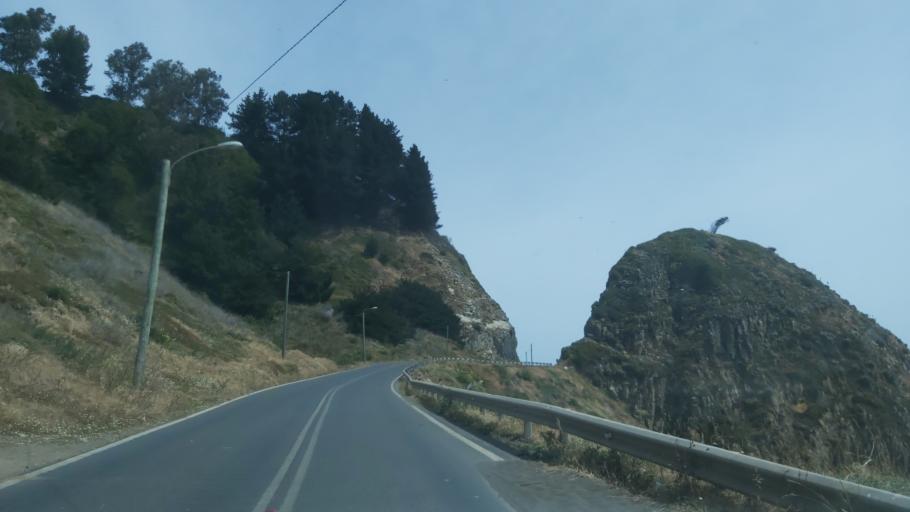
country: CL
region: Maule
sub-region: Provincia de Talca
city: Constitucion
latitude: -35.3296
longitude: -72.4327
